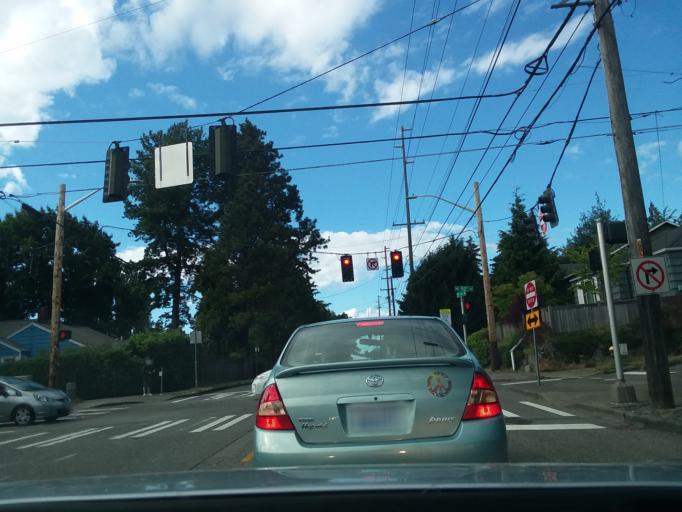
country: US
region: Washington
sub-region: King County
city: Shoreline
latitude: 47.6956
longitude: -122.3230
